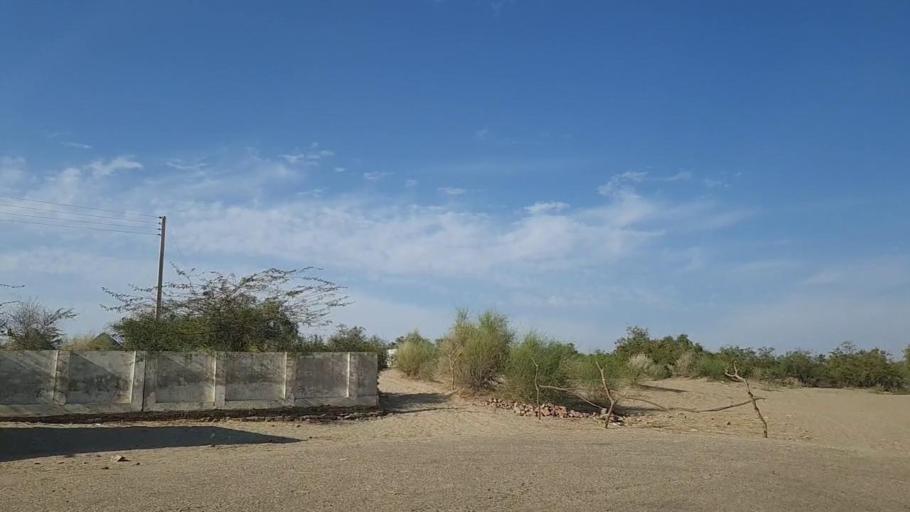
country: PK
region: Sindh
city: Naukot
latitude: 24.8659
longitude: 69.5293
